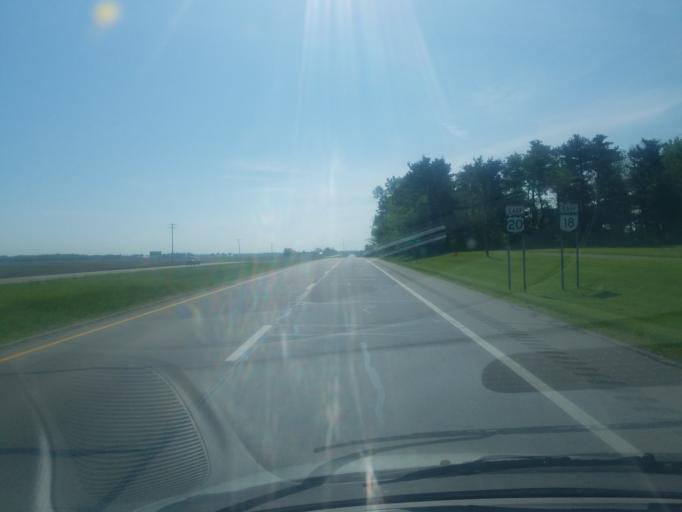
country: US
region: Ohio
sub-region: Huron County
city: Monroeville
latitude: 41.2560
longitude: -82.7455
